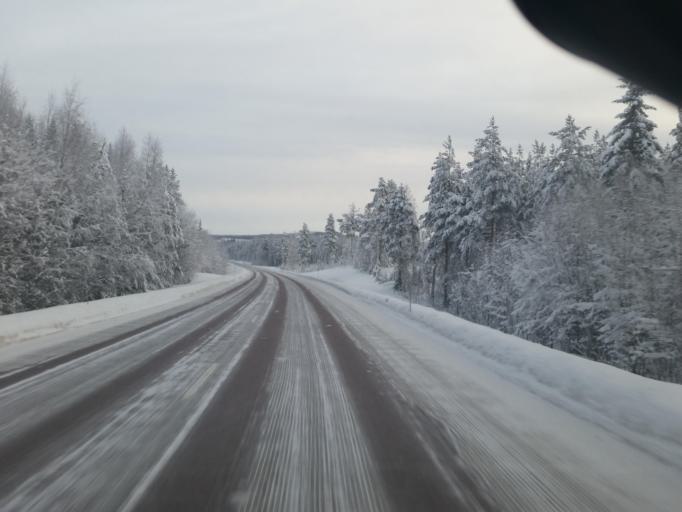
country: SE
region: Norrbotten
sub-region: Alvsbyns Kommun
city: AElvsbyn
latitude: 65.6723
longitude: 21.1487
